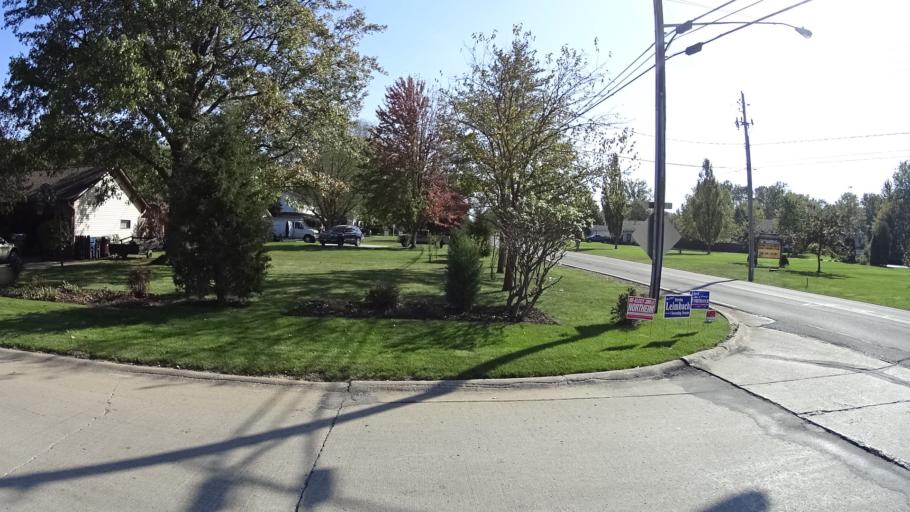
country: US
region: Ohio
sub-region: Lorain County
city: Vermilion
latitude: 41.4067
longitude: -82.3422
